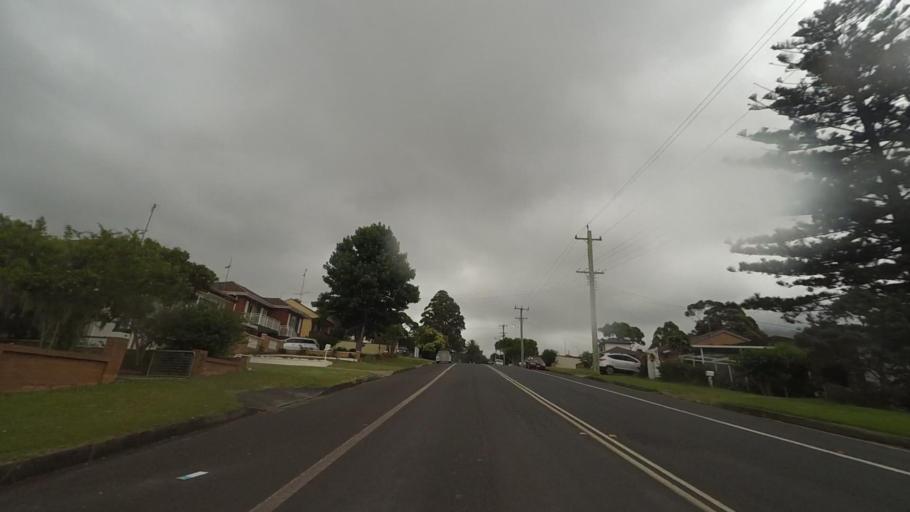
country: AU
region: New South Wales
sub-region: Wollongong
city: Cordeaux Heights
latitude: -34.4509
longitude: 150.8360
